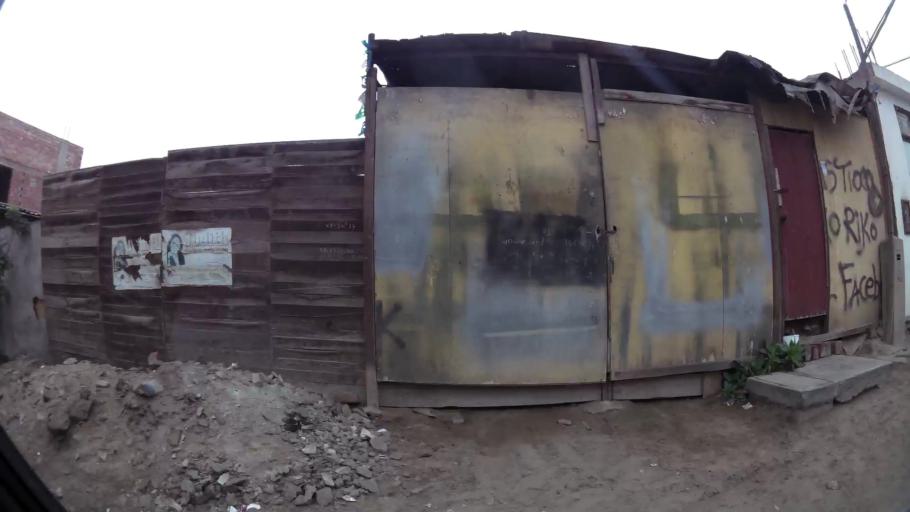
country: PE
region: Lima
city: Ventanilla
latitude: -11.8482
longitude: -77.1152
